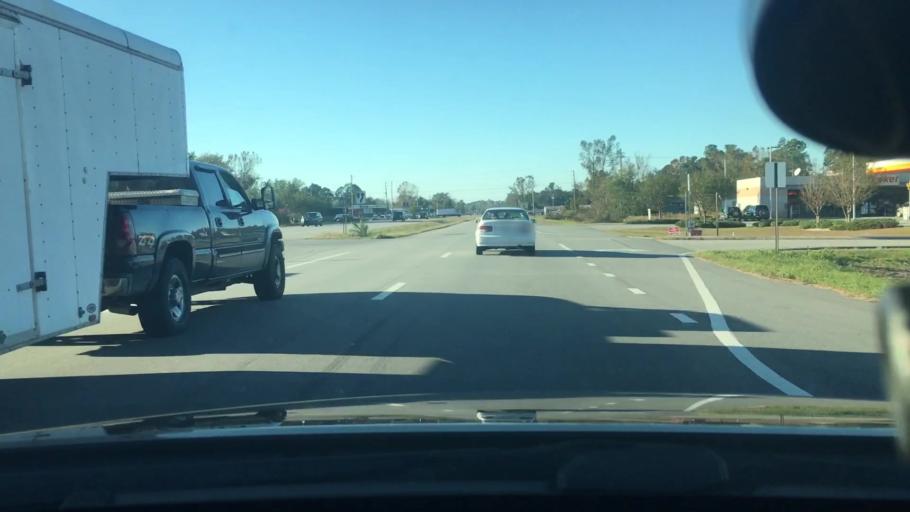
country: US
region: North Carolina
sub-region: Craven County
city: New Bern
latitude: 35.1196
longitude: -77.0167
